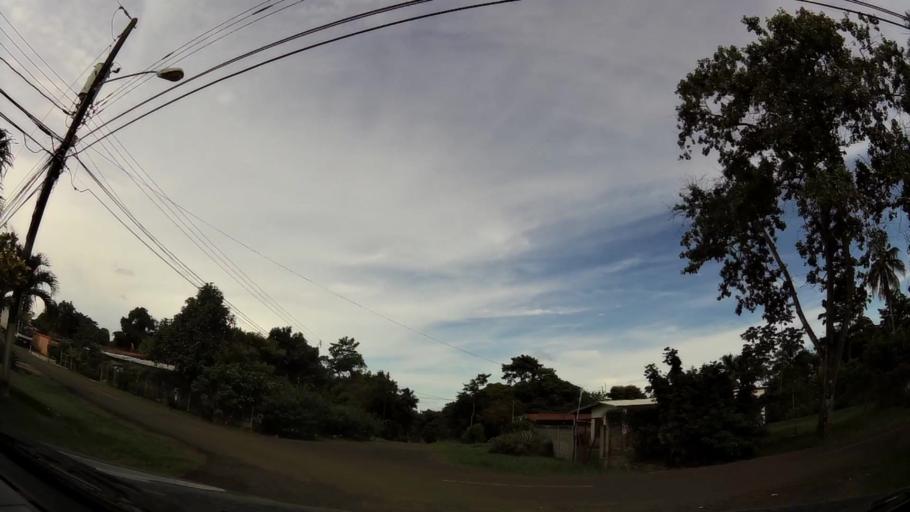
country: PA
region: Panama
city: El Coco
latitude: 8.8660
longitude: -79.8054
